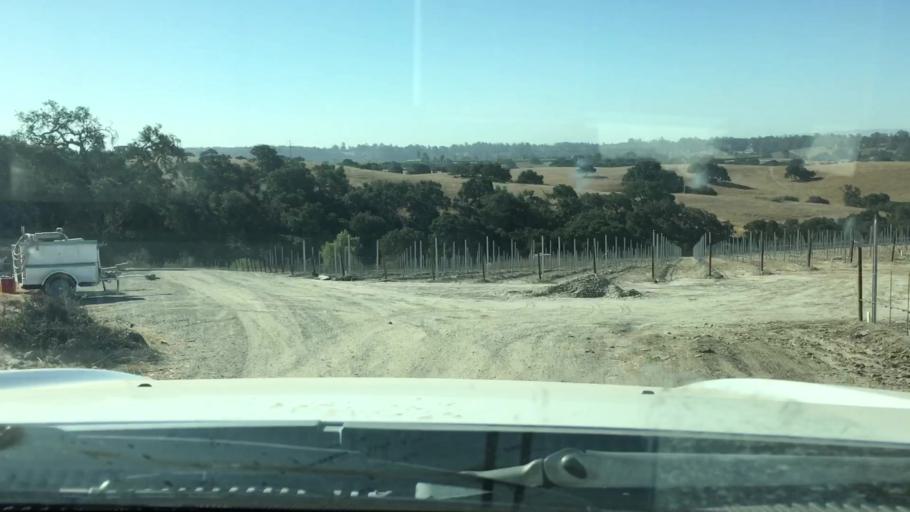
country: US
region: California
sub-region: San Luis Obispo County
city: Arroyo Grande
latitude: 35.1019
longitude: -120.5519
